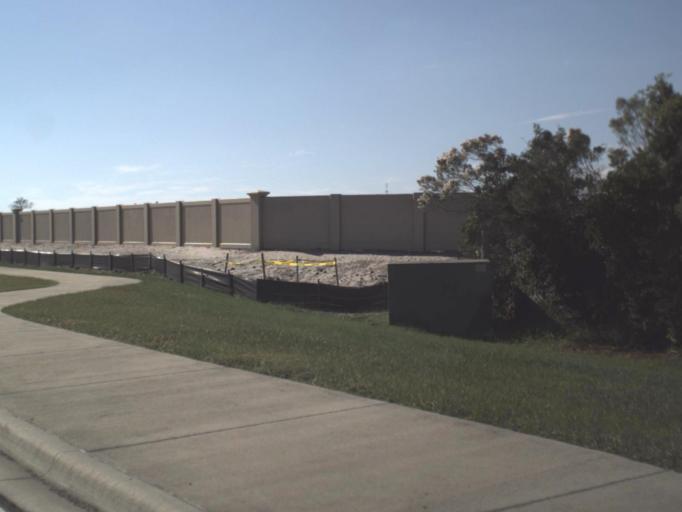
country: US
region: Florida
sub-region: Brevard County
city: South Patrick Shores
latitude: 28.1974
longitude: -80.6886
